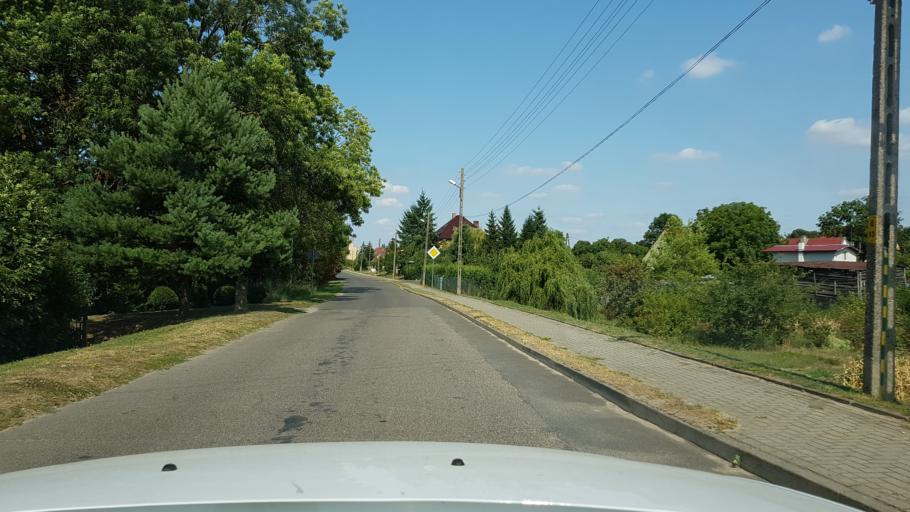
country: PL
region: West Pomeranian Voivodeship
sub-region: Powiat gryfinski
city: Moryn
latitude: 52.8488
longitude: 14.3919
